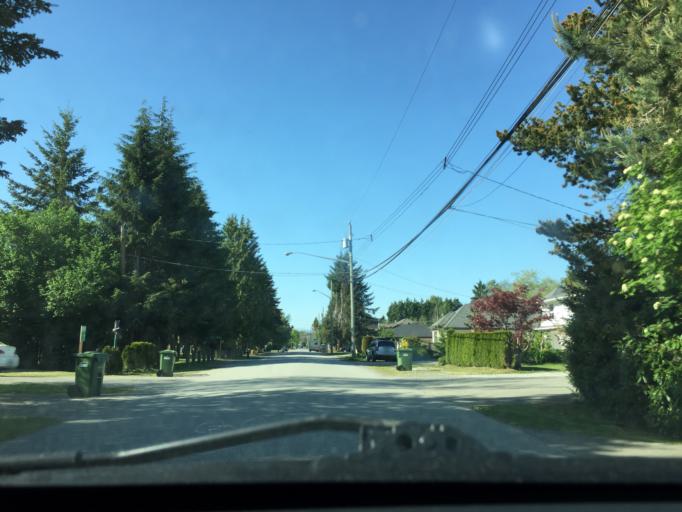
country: CA
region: British Columbia
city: Richmond
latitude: 49.1571
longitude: -123.1198
